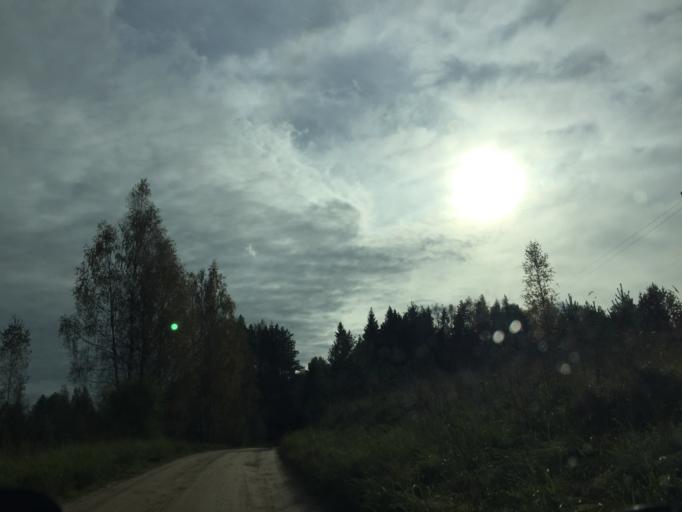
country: LV
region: Jaunpils
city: Jaunpils
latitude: 56.5747
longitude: 23.0247
